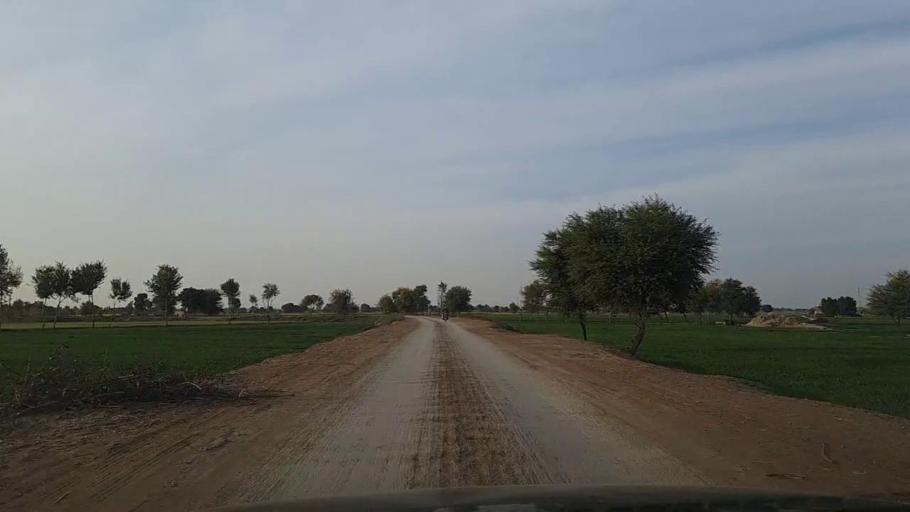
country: PK
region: Sindh
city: Jam Sahib
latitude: 26.4335
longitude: 68.5644
